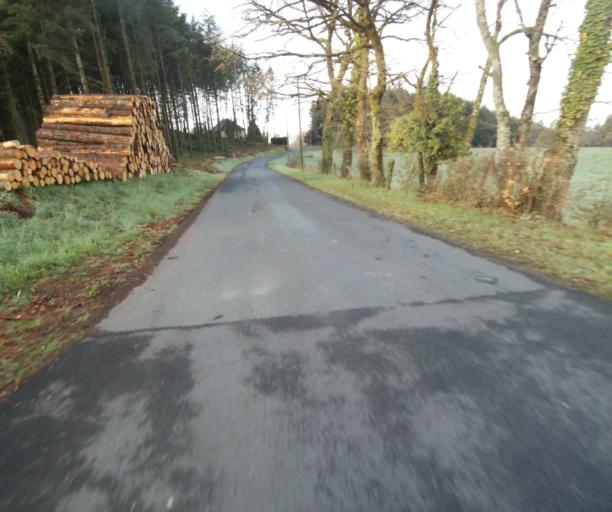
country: FR
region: Limousin
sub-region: Departement de la Correze
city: Correze
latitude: 45.3142
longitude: 1.8430
